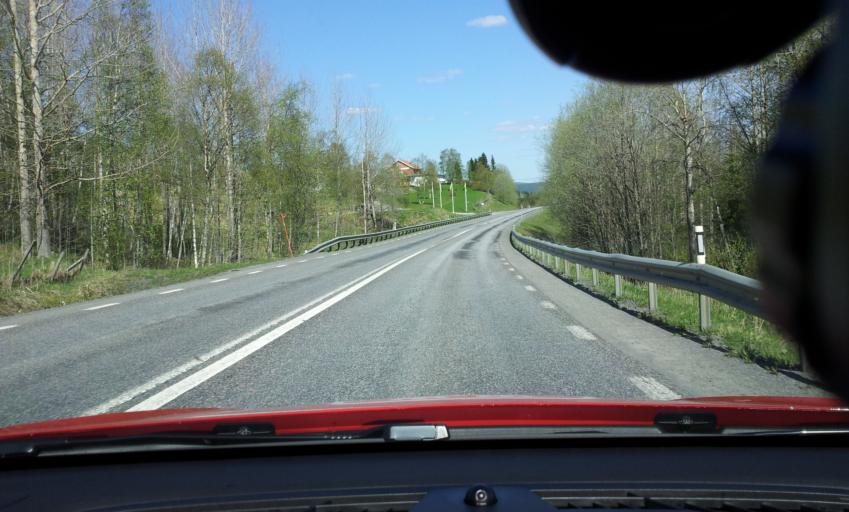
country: SE
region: Jaemtland
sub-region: Are Kommun
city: Jarpen
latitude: 63.3198
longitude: 13.3559
